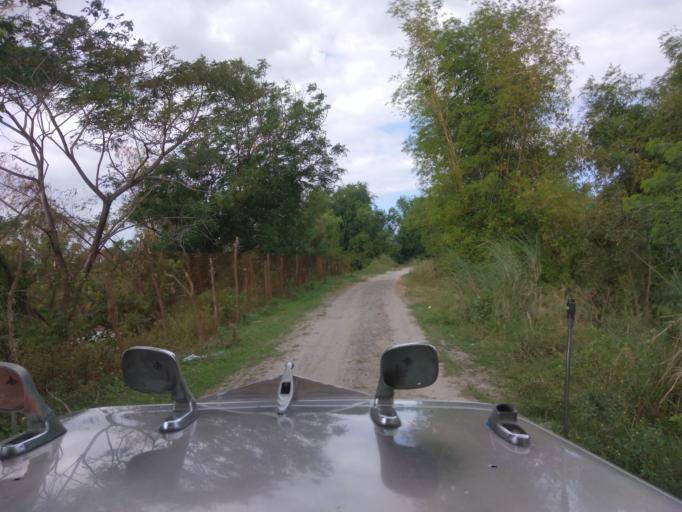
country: PH
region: Central Luzon
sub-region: Province of Pampanga
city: San Patricio
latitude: 15.1141
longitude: 120.7124
